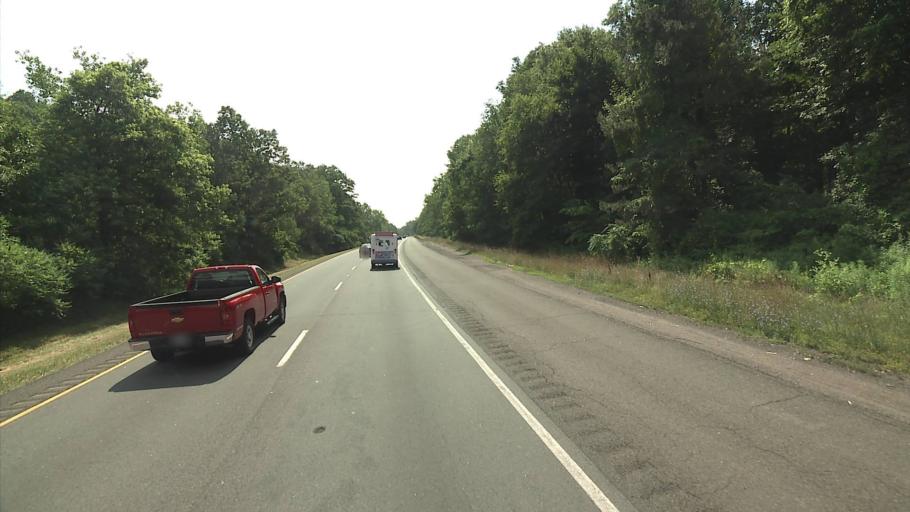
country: US
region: Connecticut
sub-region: New Haven County
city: Meriden
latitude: 41.5539
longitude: -72.8431
